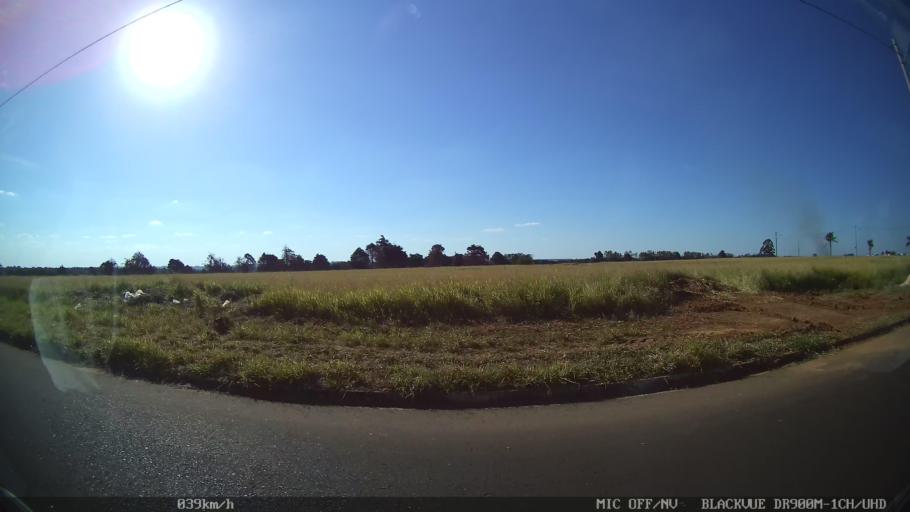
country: BR
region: Sao Paulo
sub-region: Franca
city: Franca
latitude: -20.5063
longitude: -47.4375
